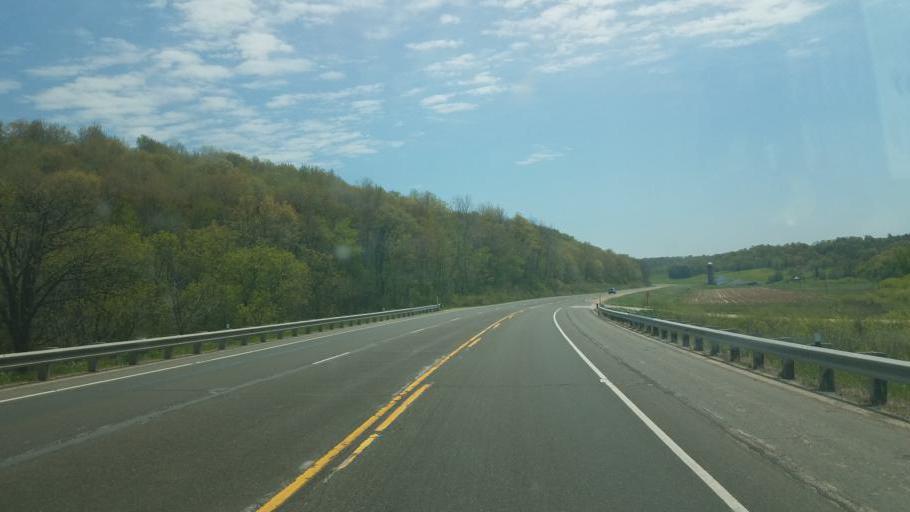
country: US
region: Wisconsin
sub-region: Monroe County
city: Tomah
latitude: 43.8863
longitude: -90.4812
